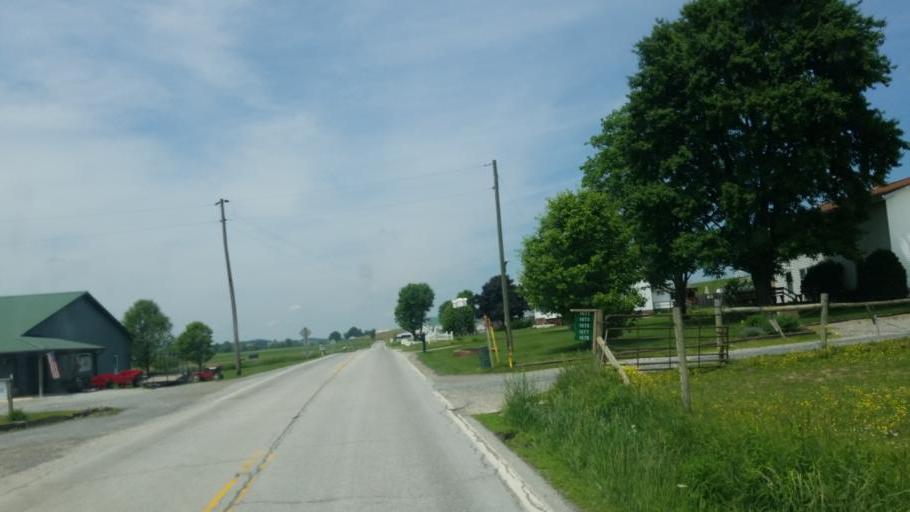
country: US
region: Ohio
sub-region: Tuscarawas County
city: Sugarcreek
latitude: 40.4695
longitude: -81.6878
